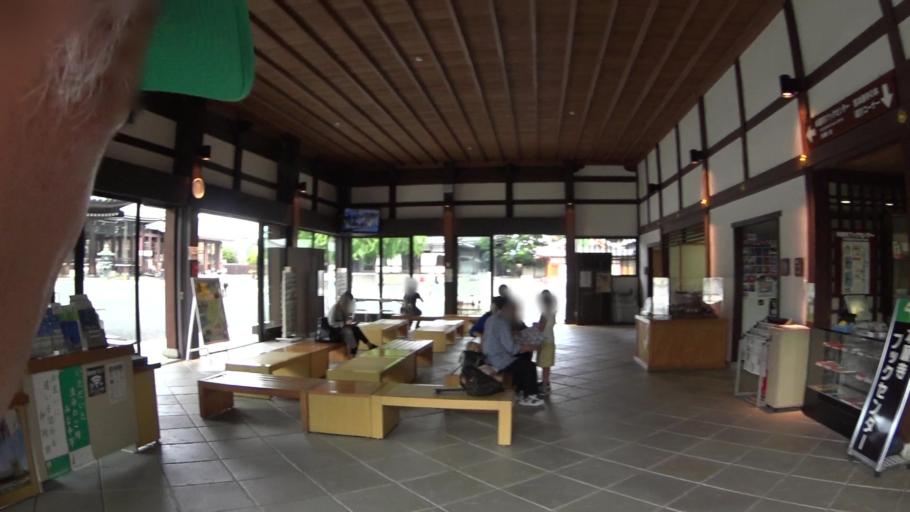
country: JP
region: Kyoto
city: Kyoto
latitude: 34.9916
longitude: 135.7524
